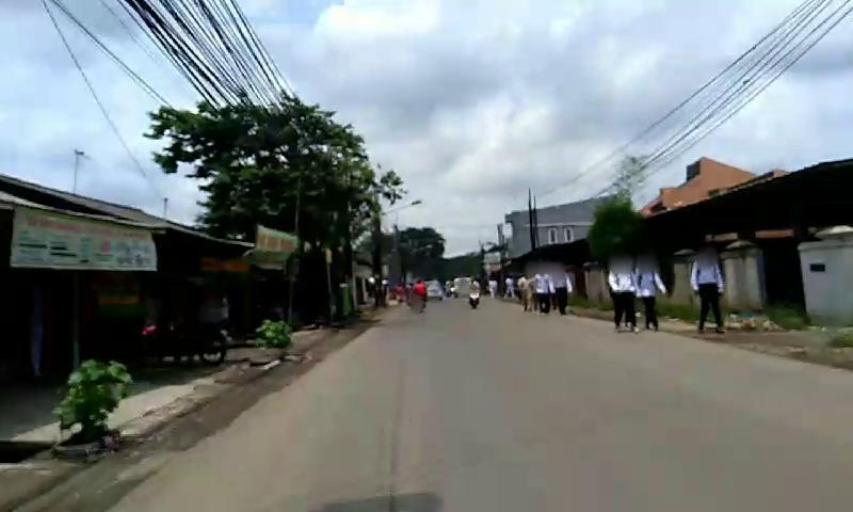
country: ID
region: West Java
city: Bekasi
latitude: -6.1979
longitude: 106.9867
